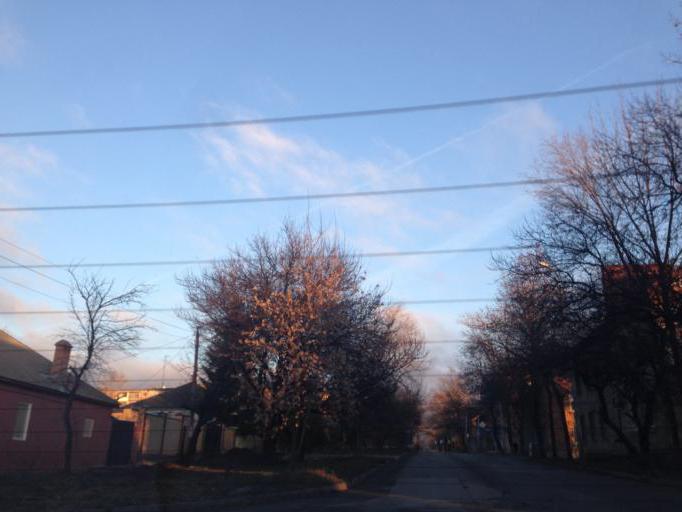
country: RU
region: Rostov
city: Rostov-na-Donu
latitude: 47.2504
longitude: 39.6835
